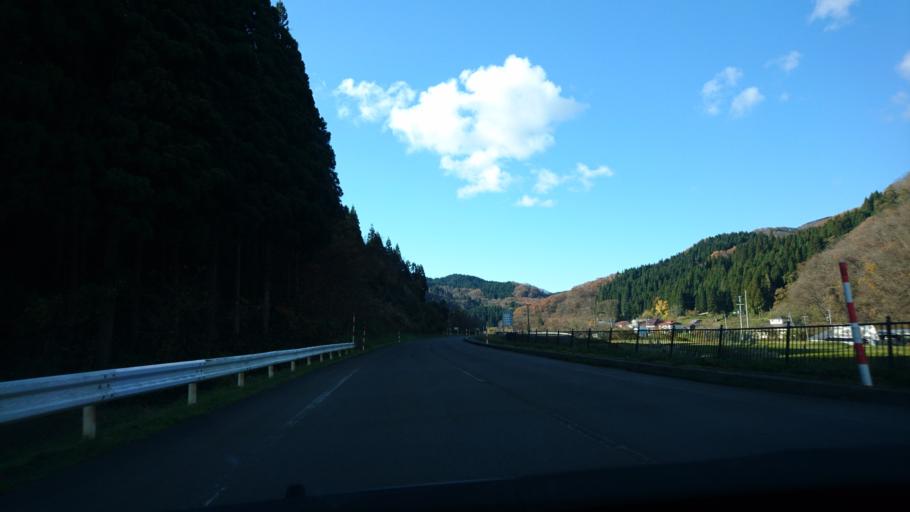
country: JP
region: Akita
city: Omagari
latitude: 39.3164
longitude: 140.2085
